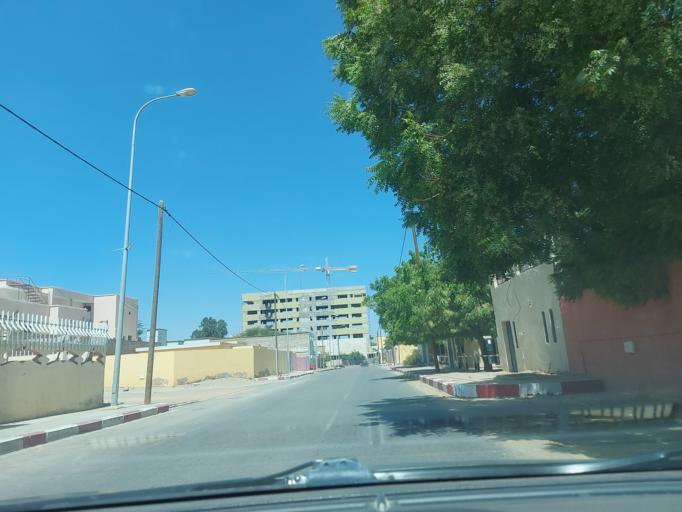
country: MR
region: Nouakchott
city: Nouakchott
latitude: 18.0929
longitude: -15.9778
